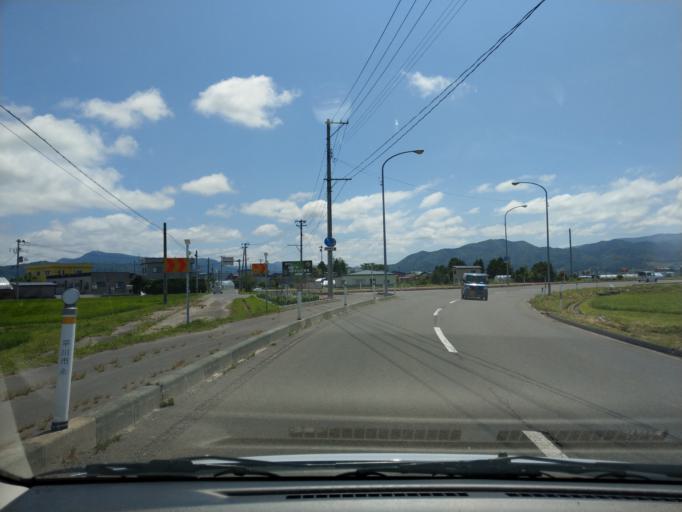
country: JP
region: Aomori
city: Kuroishi
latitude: 40.5772
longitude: 140.5516
